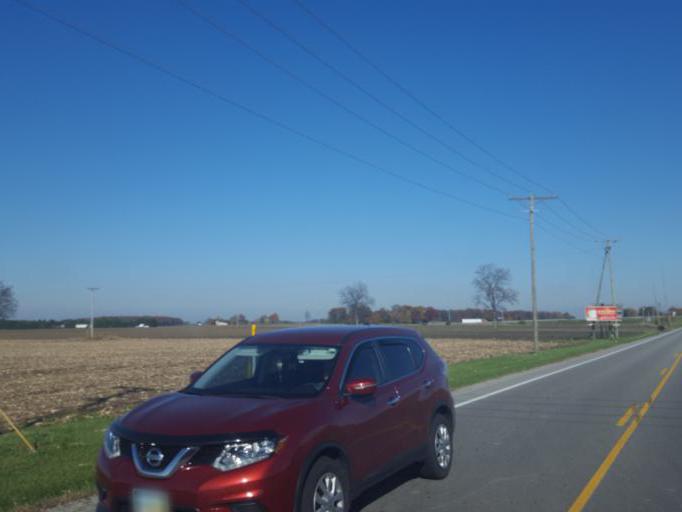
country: US
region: Ohio
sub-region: Wyandot County
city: Upper Sandusky
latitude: 40.8526
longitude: -83.2797
